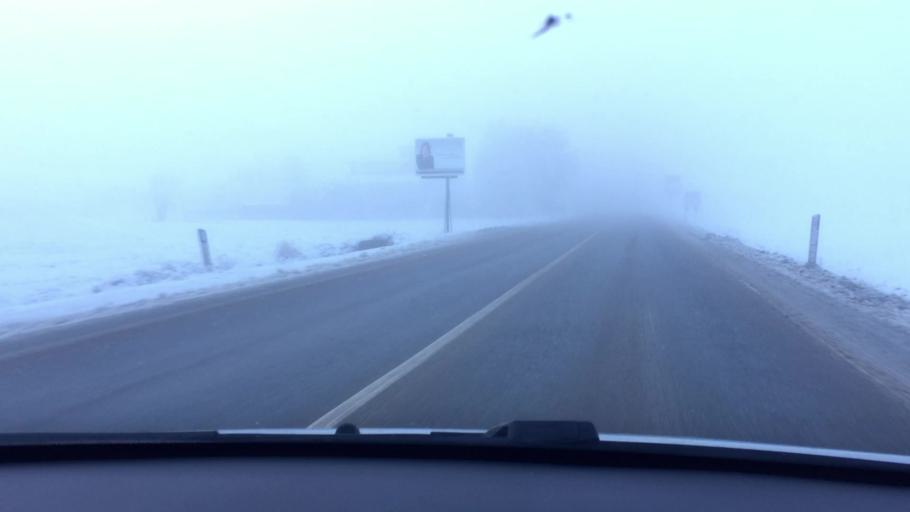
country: IT
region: Piedmont
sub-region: Provincia di Torino
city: Scalenghe
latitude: 44.8995
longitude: 7.4909
